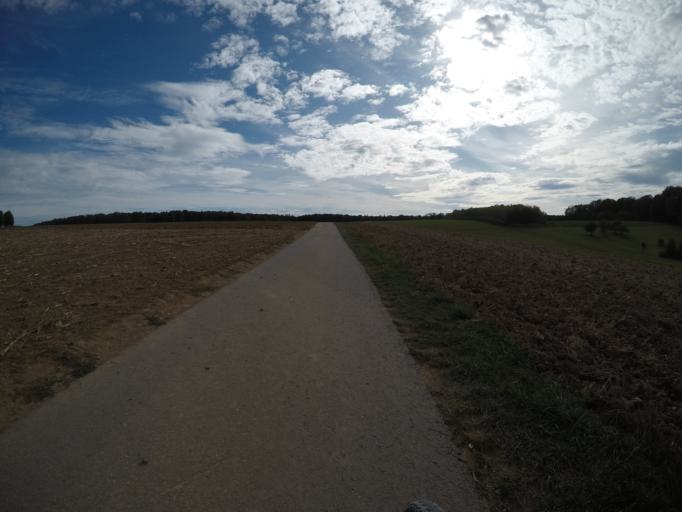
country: DE
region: Baden-Wuerttemberg
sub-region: Regierungsbezirk Stuttgart
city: Eberdingen
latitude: 48.8419
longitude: 8.9734
